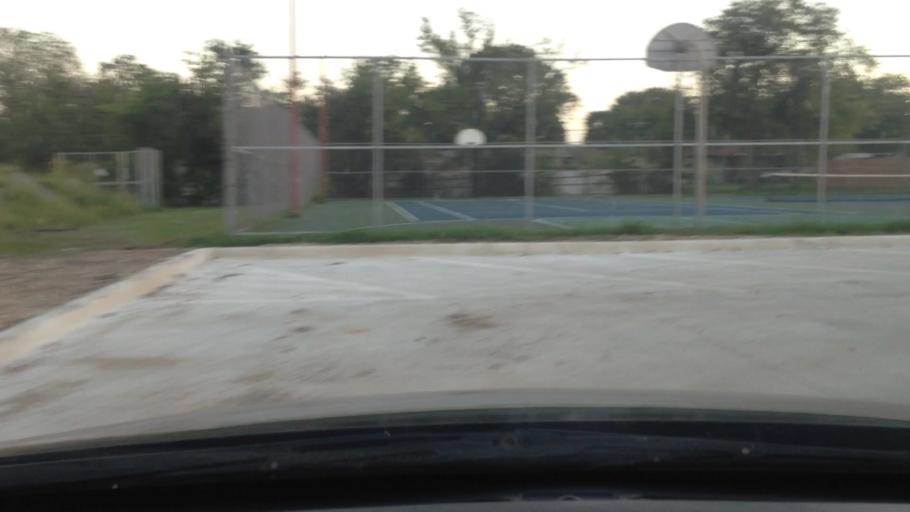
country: US
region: Texas
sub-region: Tarrant County
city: White Settlement
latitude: 32.7781
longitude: -97.4666
